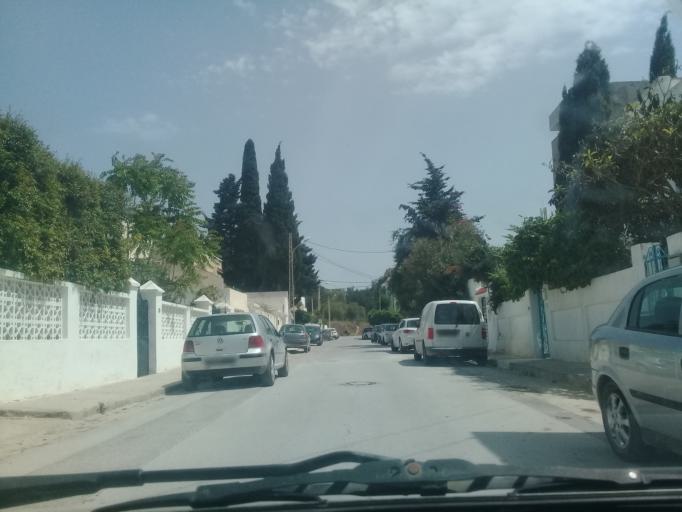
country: TN
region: Tunis
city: Al Marsa
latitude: 36.8772
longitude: 10.3311
